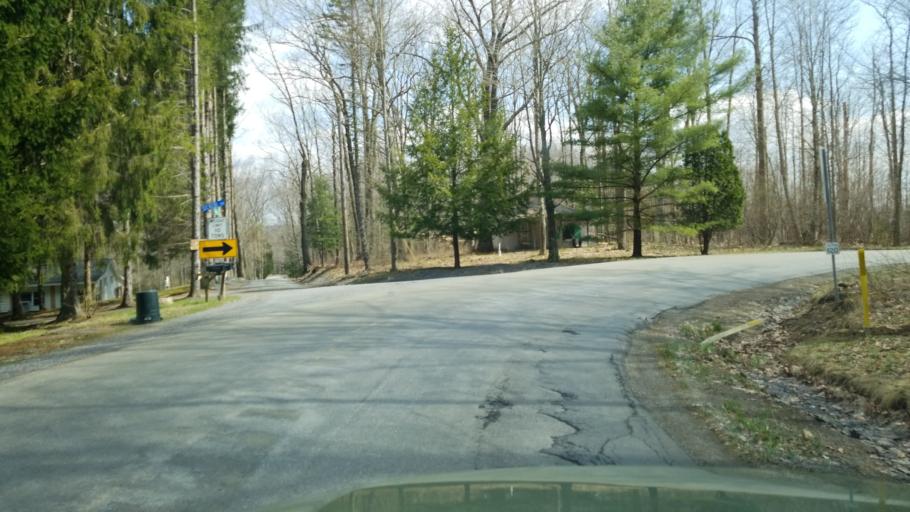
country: US
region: Pennsylvania
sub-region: Jefferson County
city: Brockway
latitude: 41.2764
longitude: -78.8373
